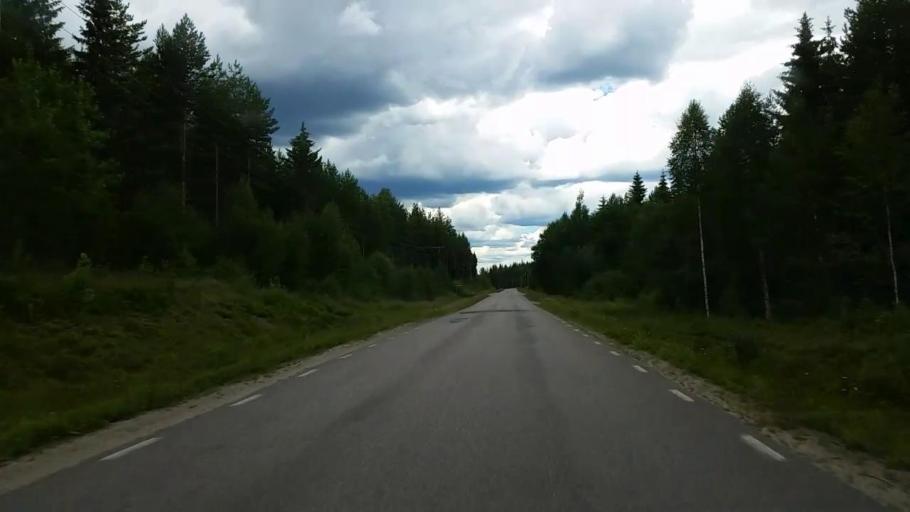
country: SE
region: Gaevleborg
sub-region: Ovanakers Kommun
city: Edsbyn
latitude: 61.4281
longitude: 15.8991
